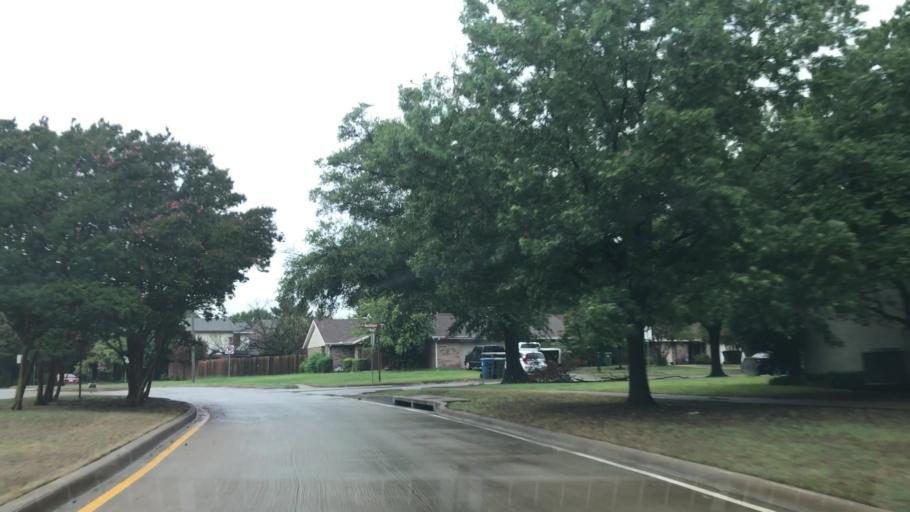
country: US
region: Texas
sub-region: Denton County
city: Highland Village
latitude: 33.0427
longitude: -97.0481
